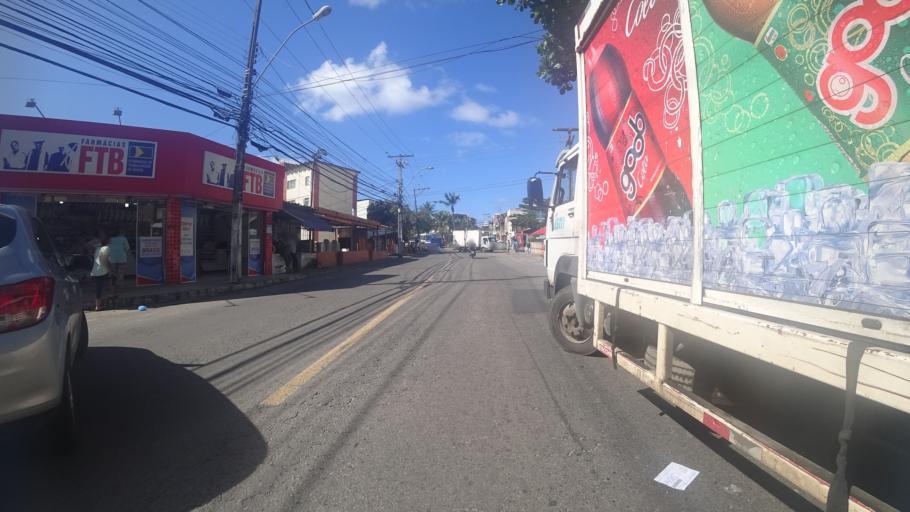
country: BR
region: Bahia
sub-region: Salvador
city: Salvador
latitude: -12.9729
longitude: -38.4344
